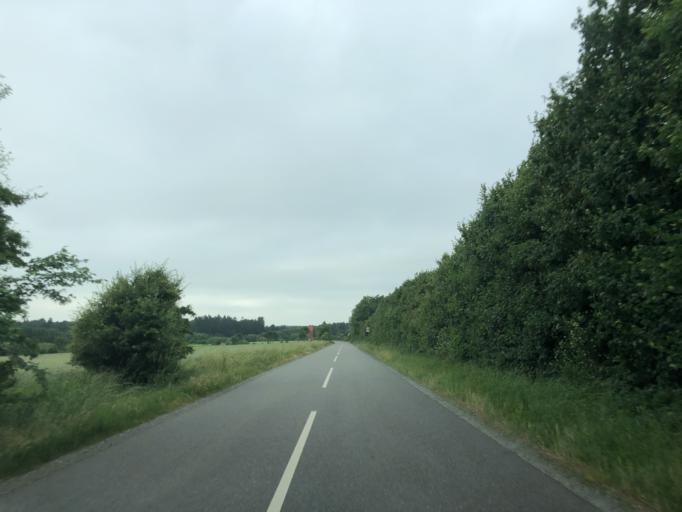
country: DK
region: Central Jutland
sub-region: Holstebro Kommune
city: Holstebro
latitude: 56.2468
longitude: 8.6246
